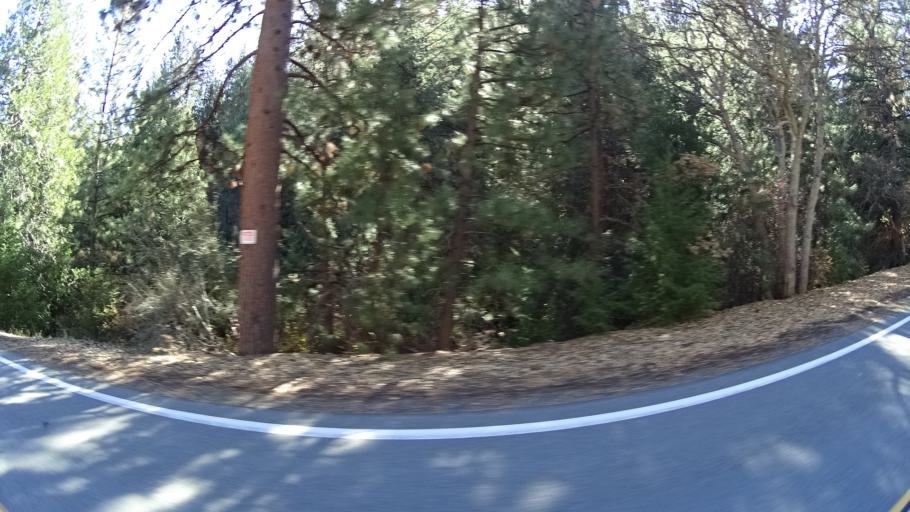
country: US
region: California
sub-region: Siskiyou County
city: Weed
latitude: 41.4577
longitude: -122.6312
